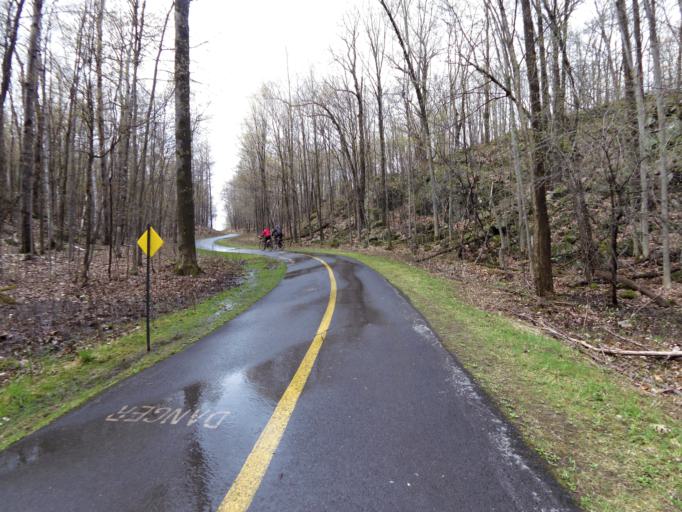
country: CA
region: Quebec
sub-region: Outaouais
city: Gatineau
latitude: 45.4645
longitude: -75.7813
